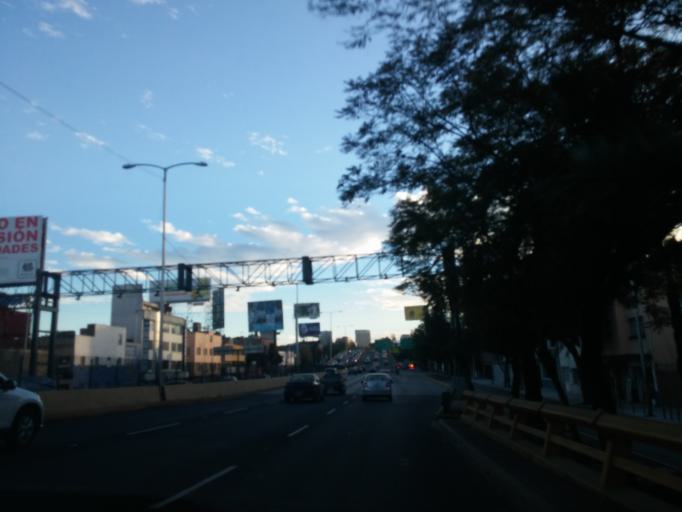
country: MX
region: Mexico City
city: Cuauhtemoc
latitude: 19.4469
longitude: -99.1651
